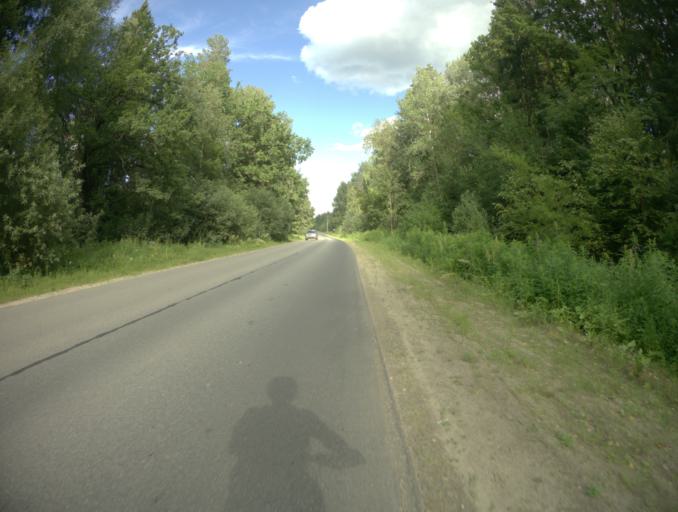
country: RU
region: Vladimir
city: Kommunar
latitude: 56.0715
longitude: 40.5269
